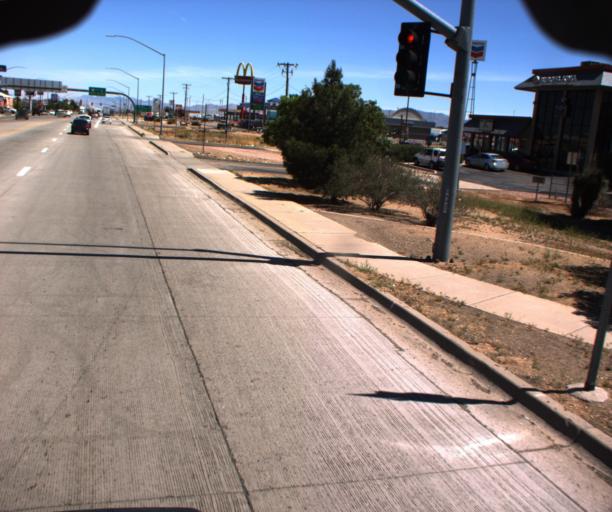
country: US
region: Arizona
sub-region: Mohave County
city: Kingman
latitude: 35.2179
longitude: -114.0100
